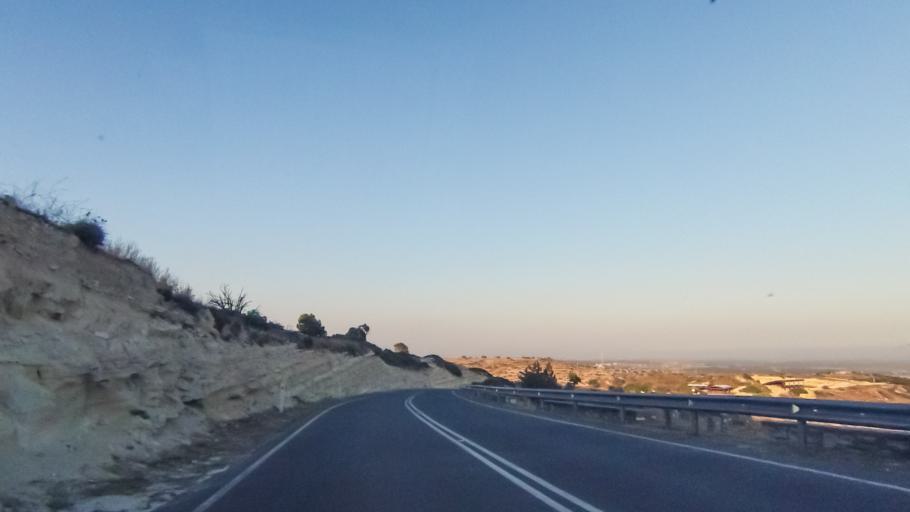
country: CY
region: Limassol
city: Erimi
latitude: 34.6698
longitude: 32.8784
